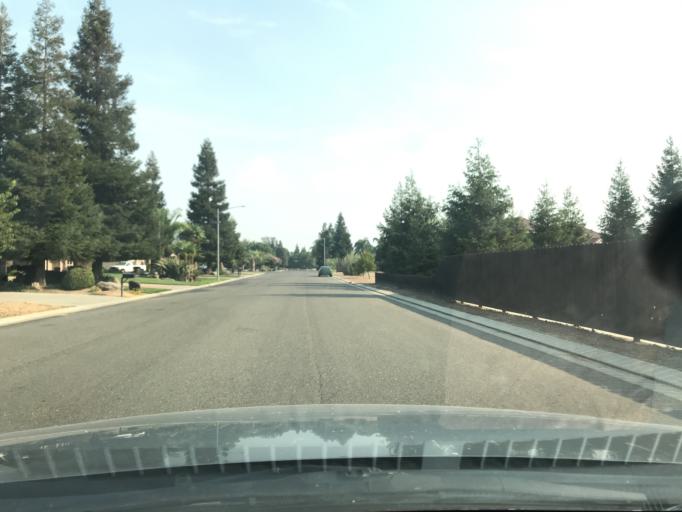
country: US
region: California
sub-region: Merced County
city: Atwater
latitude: 37.3216
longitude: -120.5976
